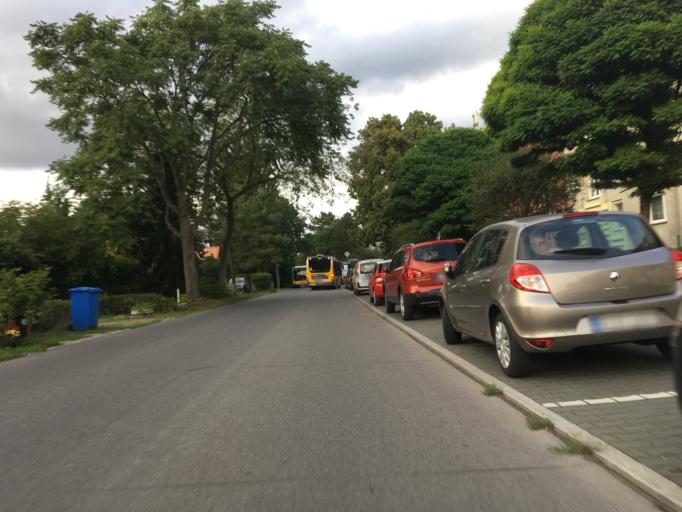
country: DE
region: Berlin
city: Johannisthal
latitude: 52.4401
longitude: 13.4942
